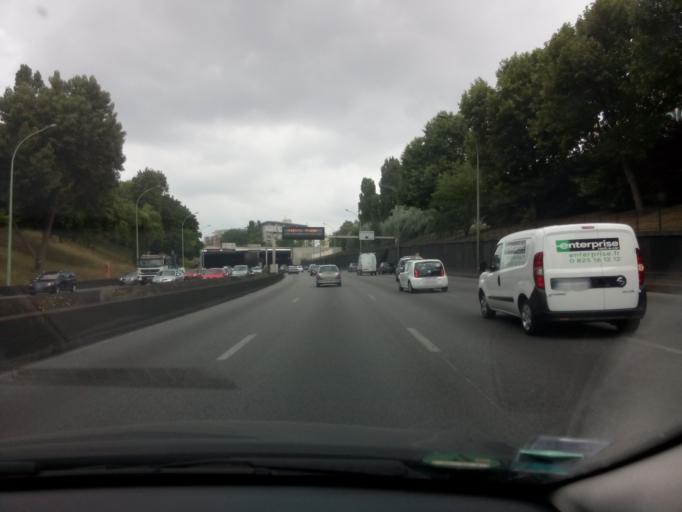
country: FR
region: Ile-de-France
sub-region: Departement de Seine-Saint-Denis
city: Bagnolet
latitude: 48.8698
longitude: 2.4133
